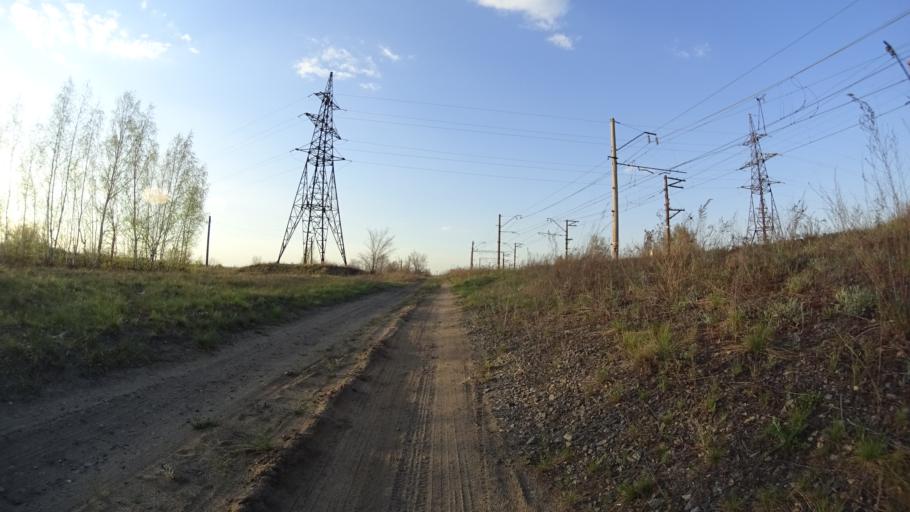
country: RU
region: Chelyabinsk
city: Troitsk
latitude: 54.0605
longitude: 61.6137
